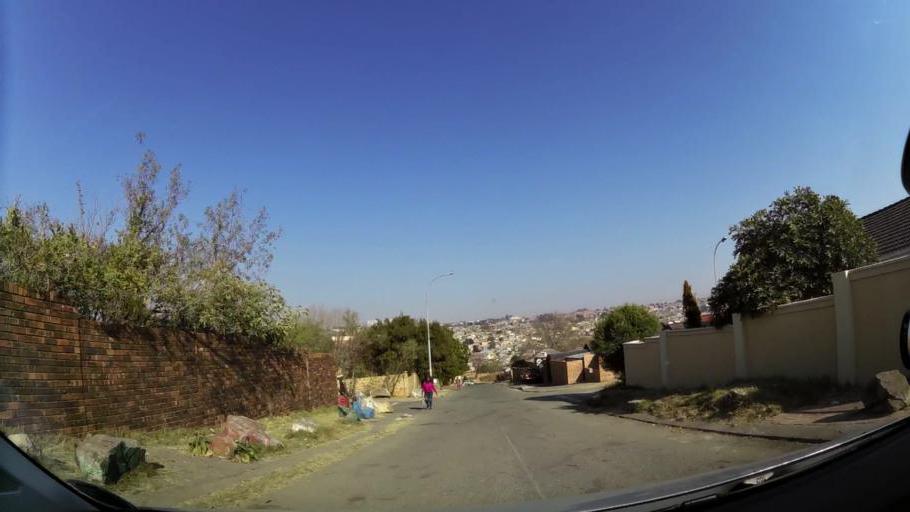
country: ZA
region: Gauteng
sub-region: City of Johannesburg Metropolitan Municipality
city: Modderfontein
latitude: -26.1070
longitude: 28.1134
